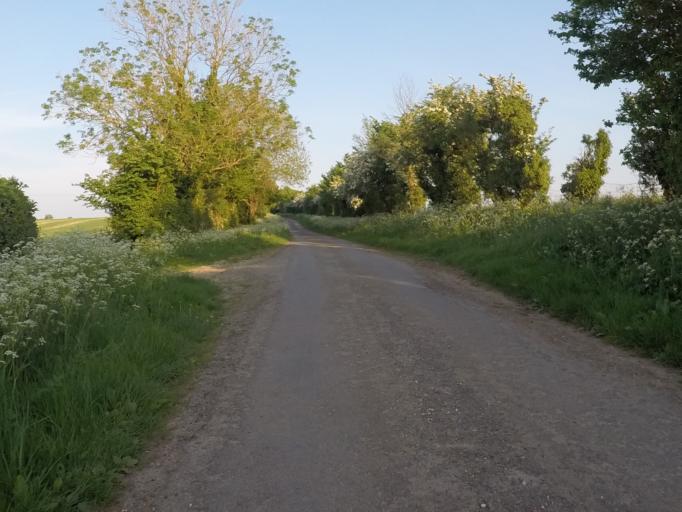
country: GB
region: England
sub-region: Oxfordshire
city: Shipton under Wychwood
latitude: 51.8562
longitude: -1.5499
